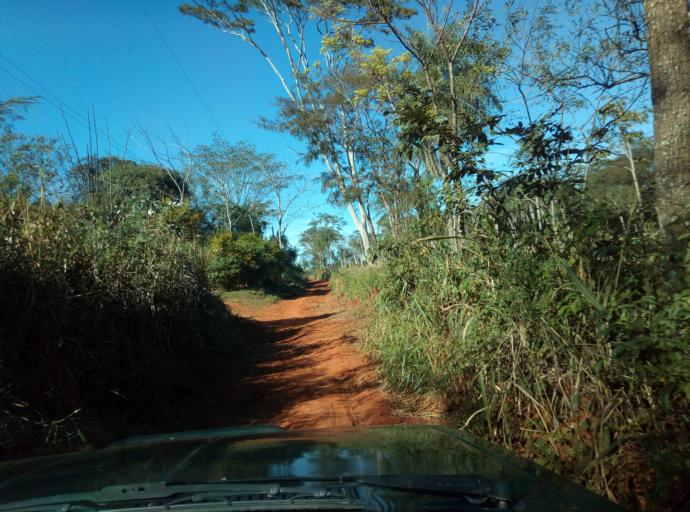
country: PY
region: Caaguazu
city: Doctor Cecilio Baez
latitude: -25.1806
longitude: -56.2423
